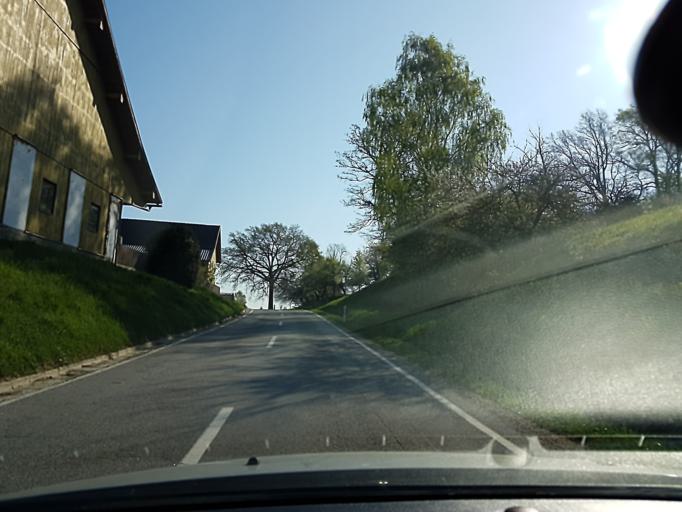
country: DE
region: Bavaria
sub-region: Lower Bavaria
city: Altfraunhofen
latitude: 48.4504
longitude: 12.1808
